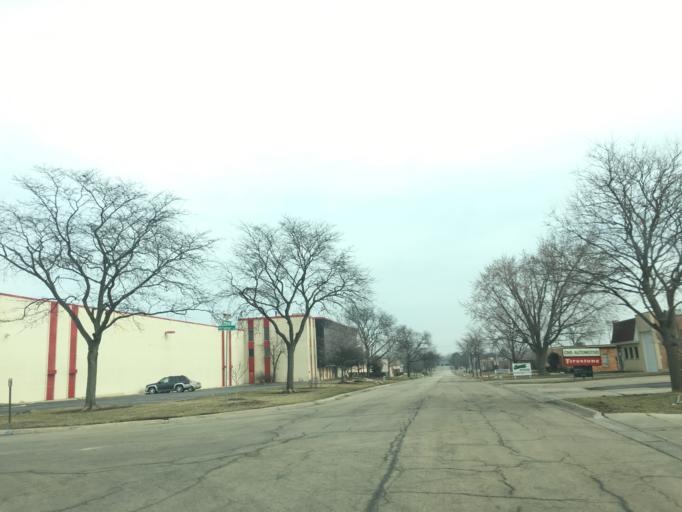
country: US
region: Illinois
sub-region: Cook County
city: Hoffman Estates
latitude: 42.0679
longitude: -88.0604
